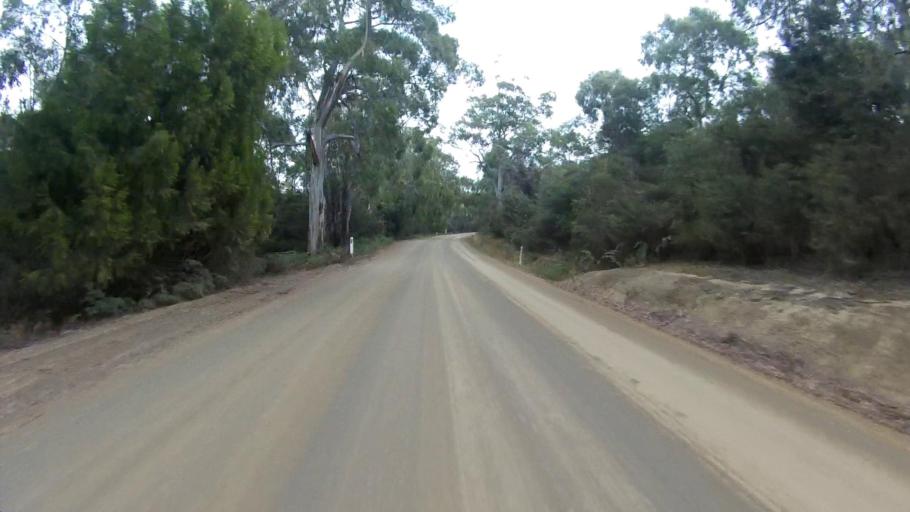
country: AU
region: Tasmania
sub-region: Huon Valley
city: Cygnet
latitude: -43.2247
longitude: 147.0960
